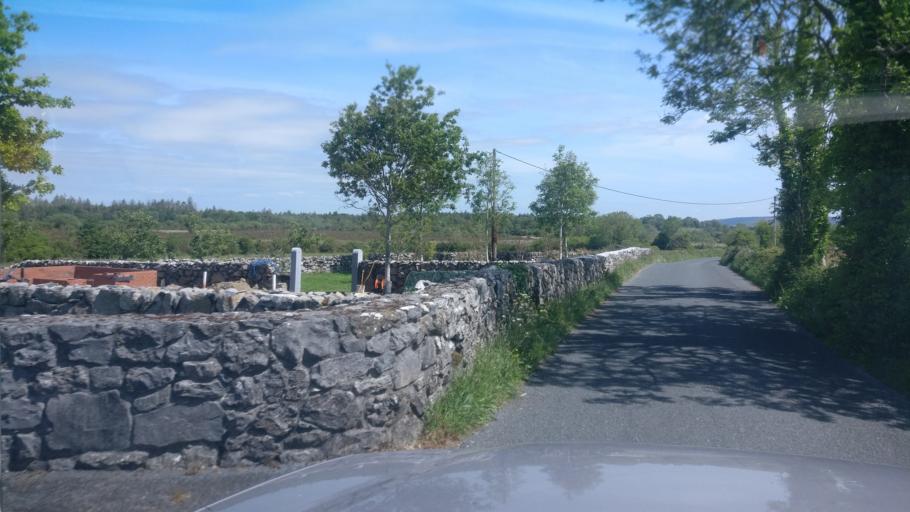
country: IE
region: Connaught
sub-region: County Galway
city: Gort
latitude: 53.1233
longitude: -8.7871
